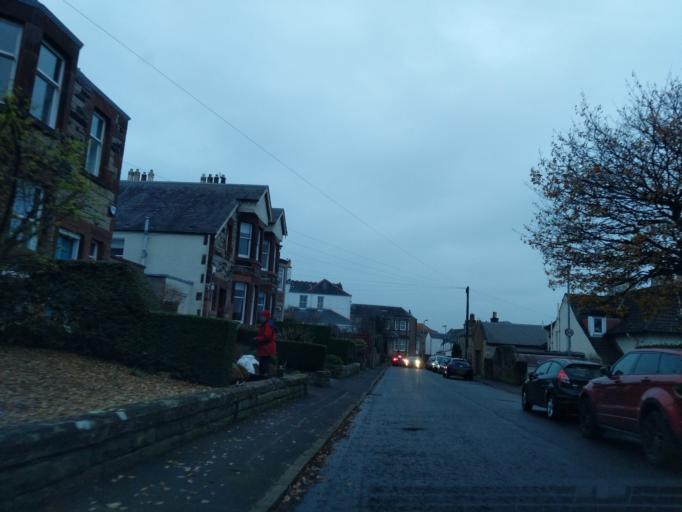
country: GB
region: Scotland
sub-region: Edinburgh
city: Colinton
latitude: 55.9456
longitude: -3.2819
